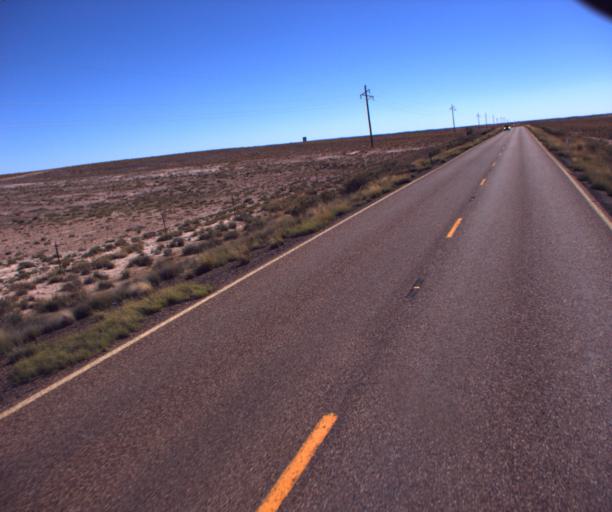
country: US
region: Arizona
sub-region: Navajo County
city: Holbrook
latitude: 35.0759
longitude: -110.0995
